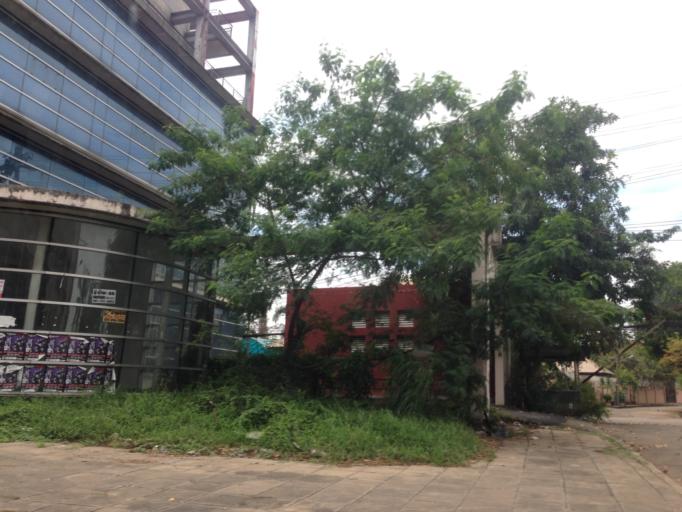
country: TH
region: Nonthaburi
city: Pak Kret
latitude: 13.9170
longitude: 100.5405
